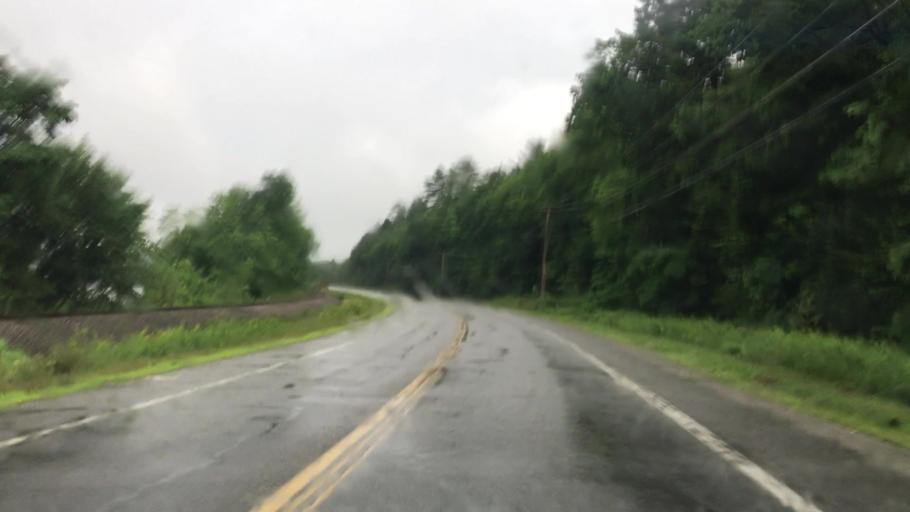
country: US
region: Maine
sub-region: Kennebec County
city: Pittston
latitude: 44.2027
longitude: -69.7646
